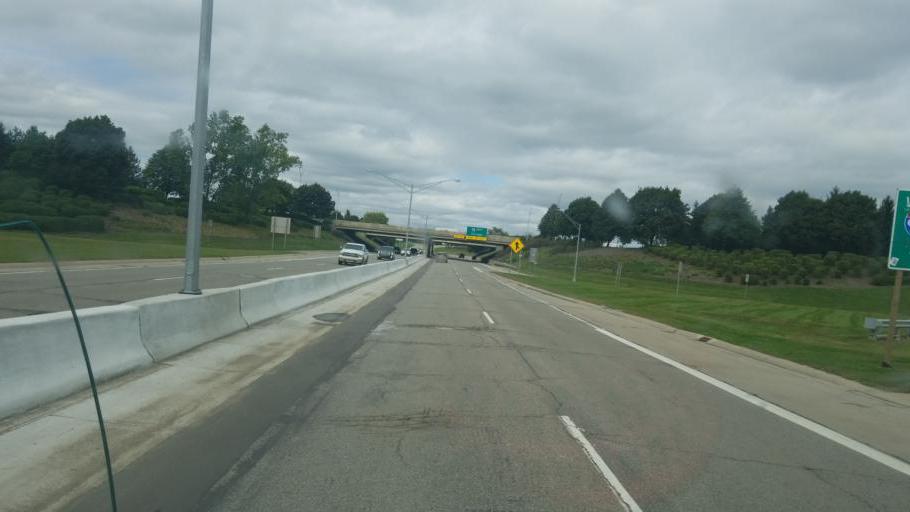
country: US
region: Michigan
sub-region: Wayne County
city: Romulus
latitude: 42.2372
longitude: -83.3408
